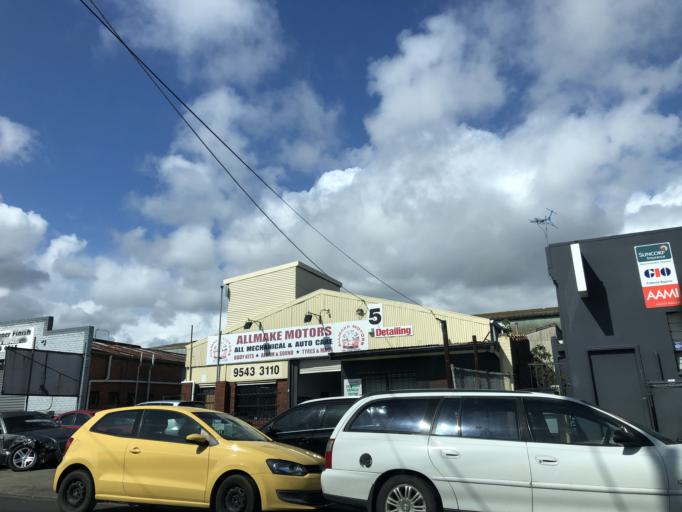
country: AU
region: Victoria
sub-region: Kingston
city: Clayton South
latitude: -37.9296
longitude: 145.1206
